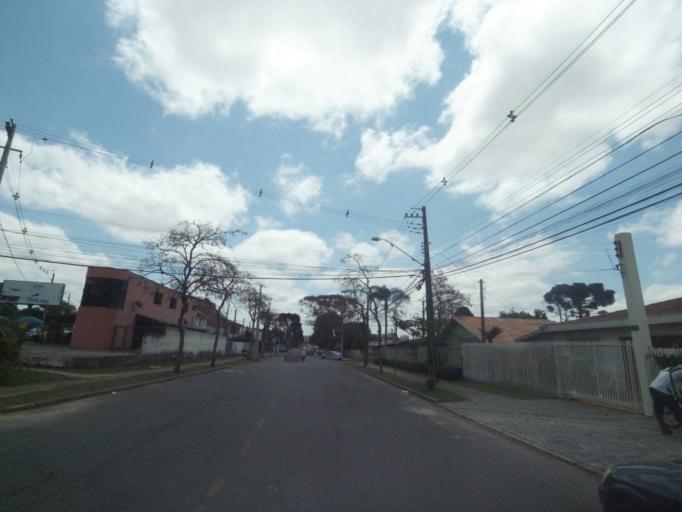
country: BR
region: Parana
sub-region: Curitiba
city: Curitiba
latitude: -25.3991
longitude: -49.2305
